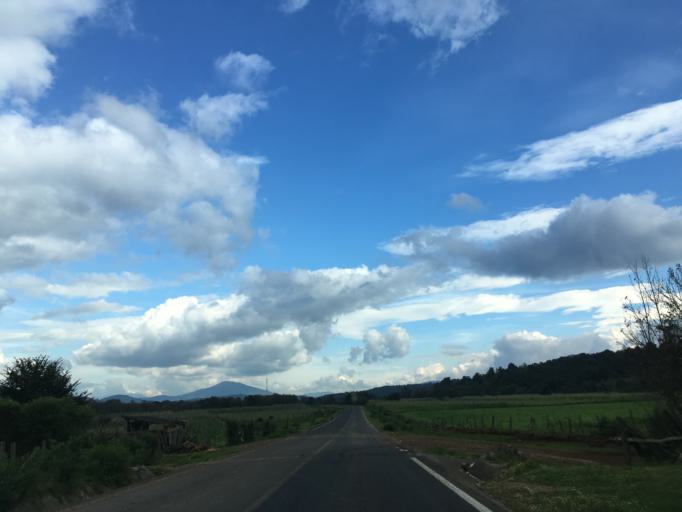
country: MX
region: Michoacan
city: Pichataro
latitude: 19.5729
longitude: -101.8146
